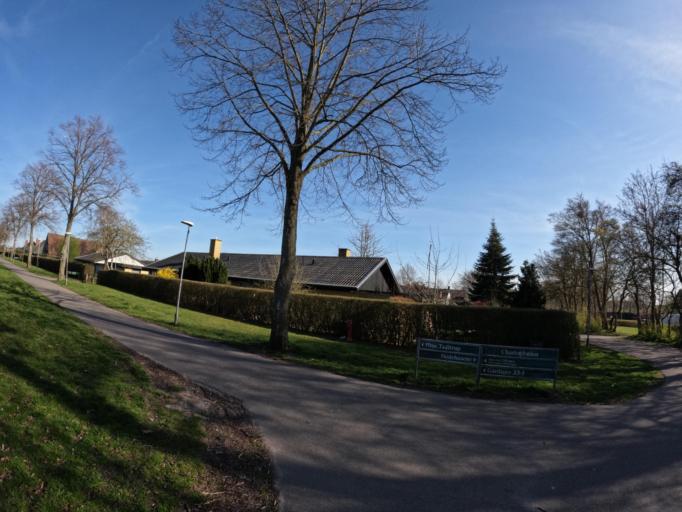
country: DK
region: Capital Region
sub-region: Hoje-Taastrup Kommune
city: Flong
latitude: 55.6480
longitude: 12.2210
